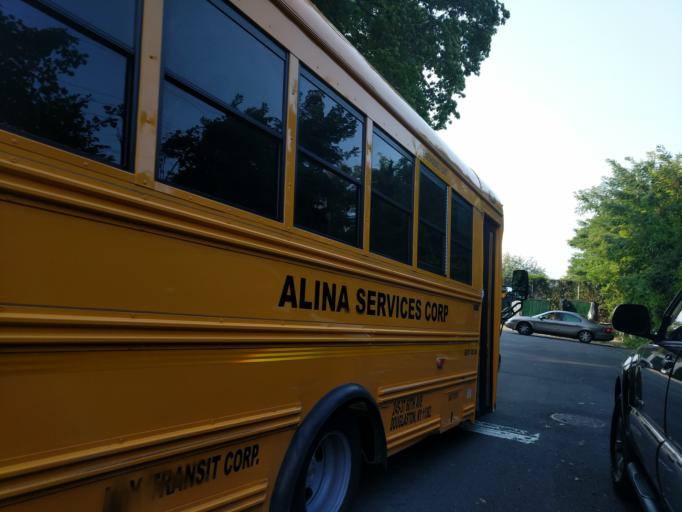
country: US
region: New York
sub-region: Queens County
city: Long Island City
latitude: 40.7593
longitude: -73.9046
